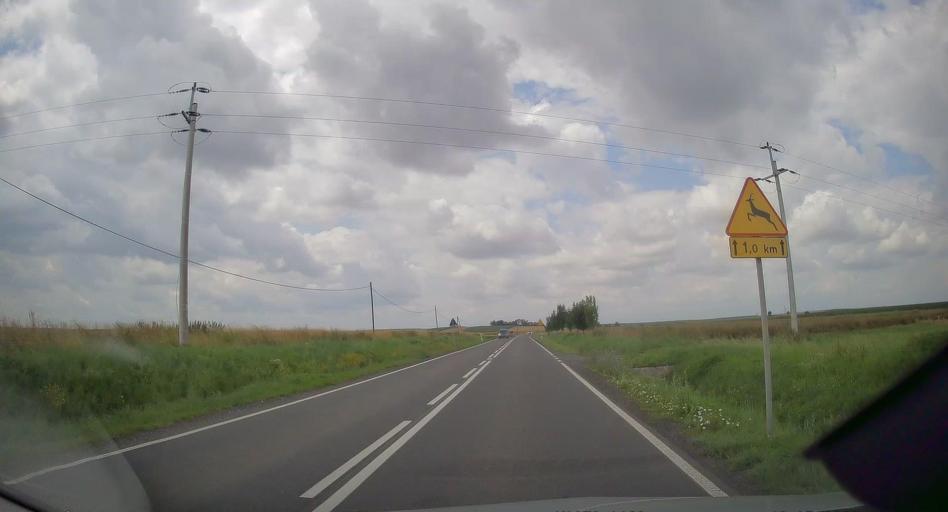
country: PL
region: Opole Voivodeship
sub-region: Powiat prudnicki
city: Glogowek
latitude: 50.3528
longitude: 17.8403
